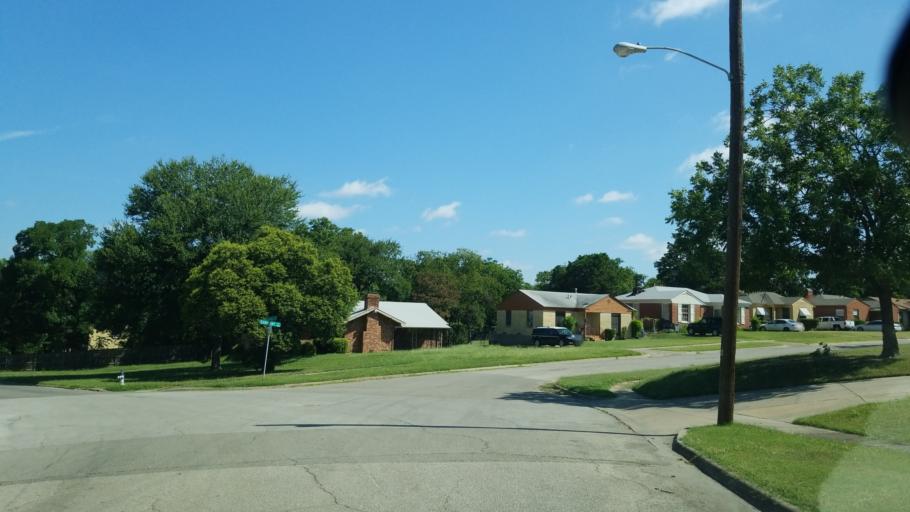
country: US
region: Texas
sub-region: Dallas County
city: Dallas
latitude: 32.7321
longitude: -96.7987
